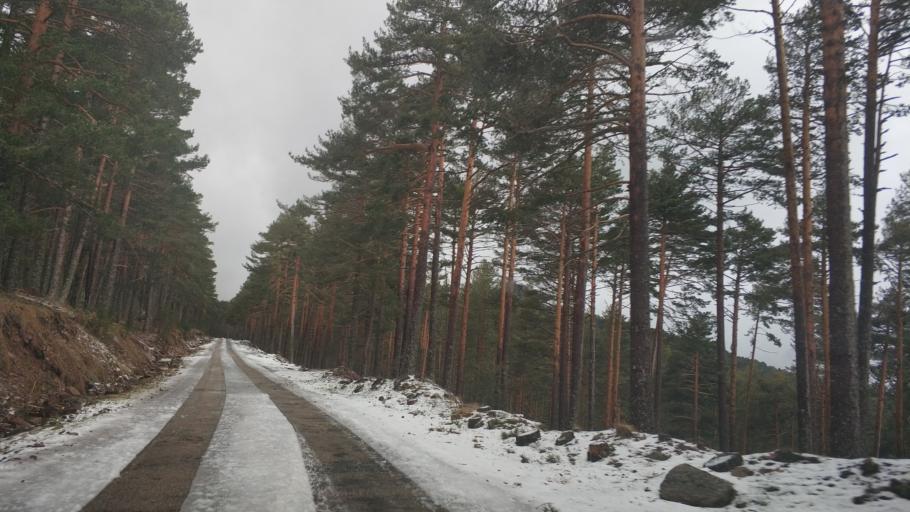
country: ES
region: Castille and Leon
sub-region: Provincia de Burgos
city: Neila
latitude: 42.0474
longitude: -3.0271
